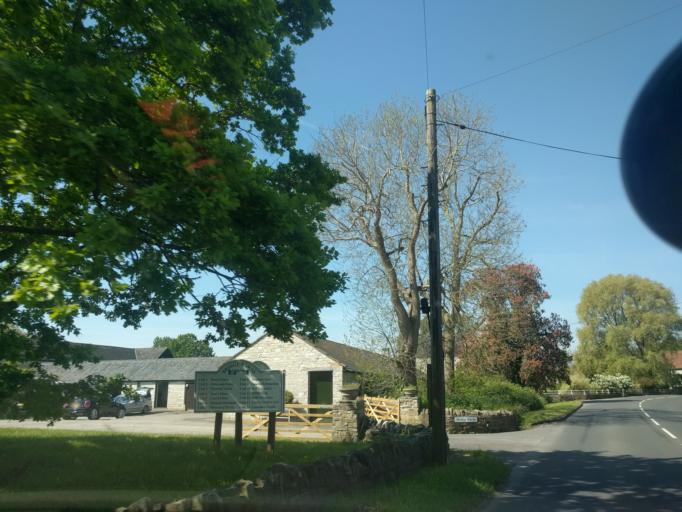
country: GB
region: England
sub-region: Somerset
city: Langport
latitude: 51.0333
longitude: -2.7720
